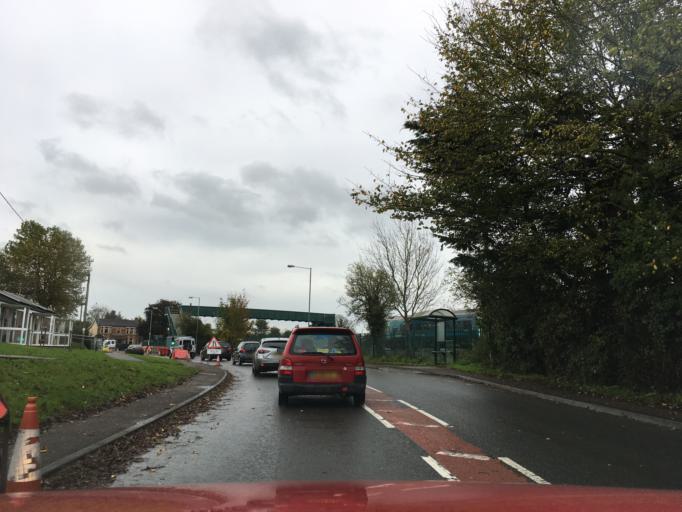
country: GB
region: Wales
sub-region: Monmouthshire
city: Magor
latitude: 51.5781
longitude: -2.8212
